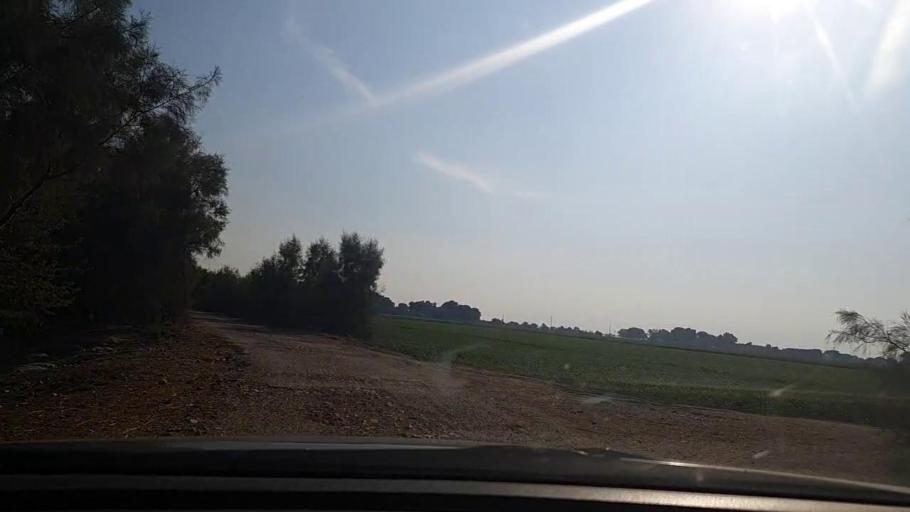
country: PK
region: Sindh
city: Sehwan
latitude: 26.3092
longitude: 68.0010
